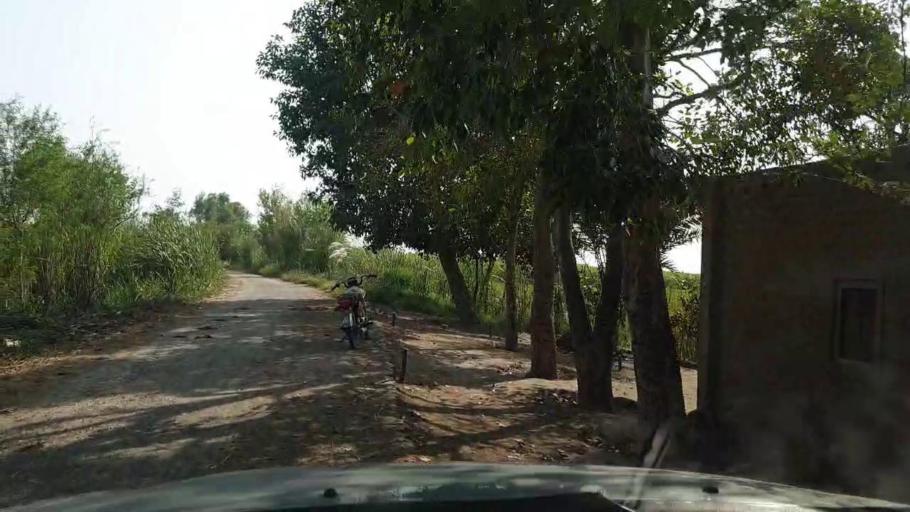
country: PK
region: Sindh
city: Bulri
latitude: 24.9020
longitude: 68.3762
